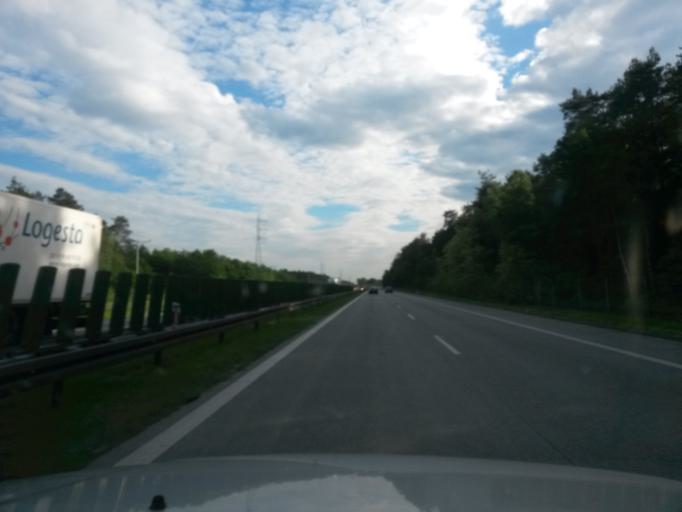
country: PL
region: Lodz Voivodeship
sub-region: Powiat piotrkowski
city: Moszczenica
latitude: 51.4553
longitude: 19.7732
